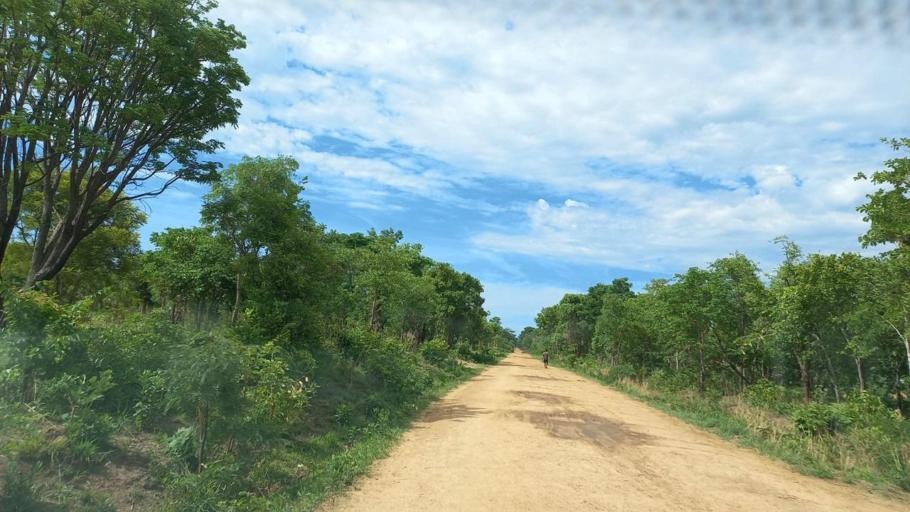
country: ZM
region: North-Western
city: Kabompo
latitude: -13.5233
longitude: 24.3825
